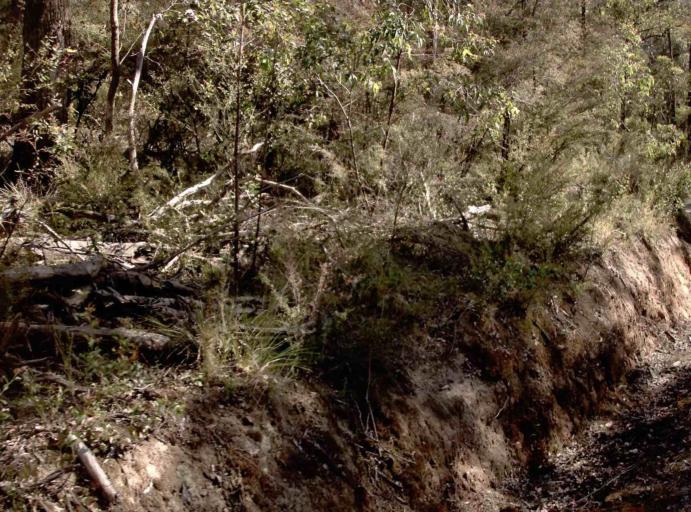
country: AU
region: Victoria
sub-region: East Gippsland
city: Lakes Entrance
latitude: -37.4951
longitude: 148.5558
